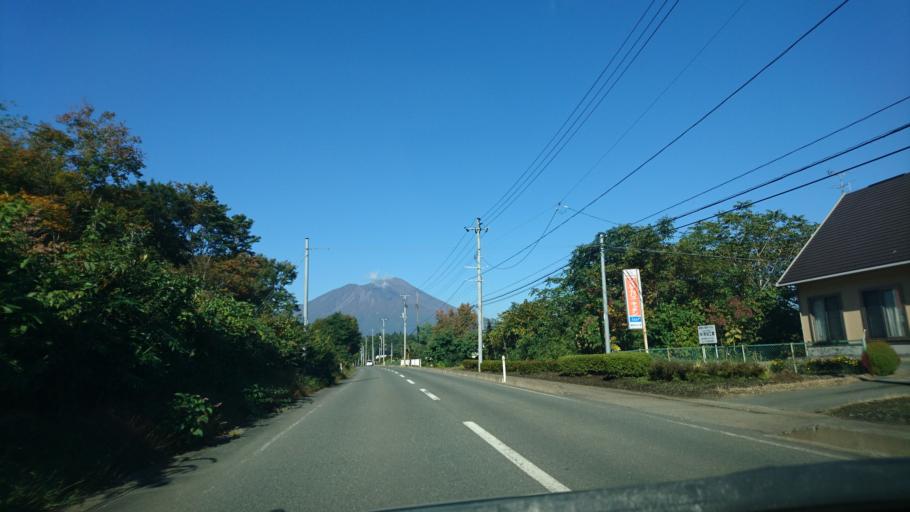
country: JP
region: Iwate
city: Morioka-shi
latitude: 39.8106
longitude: 141.1357
